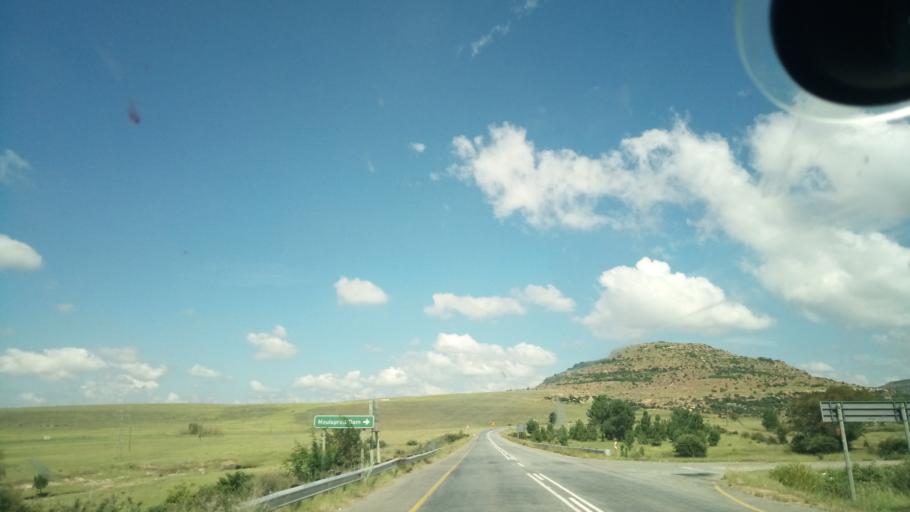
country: ZA
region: Orange Free State
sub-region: Thabo Mofutsanyana District Municipality
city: Ficksburg
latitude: -28.8922
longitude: 27.8520
